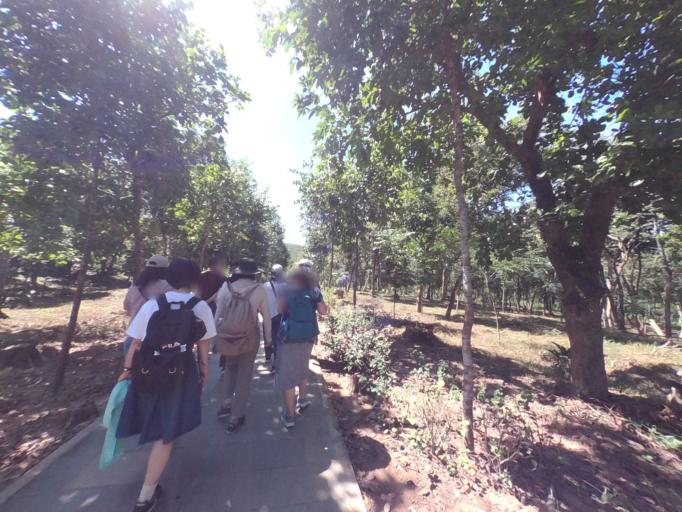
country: VN
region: Quang Nam
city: Dai Loc
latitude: 15.7671
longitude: 108.1216
